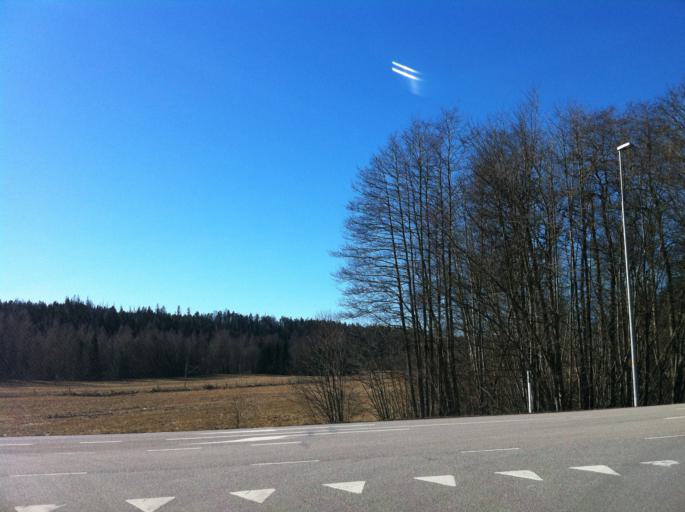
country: SE
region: Vaestra Goetaland
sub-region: Grastorps Kommun
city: Graestorp
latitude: 58.4124
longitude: 12.5935
